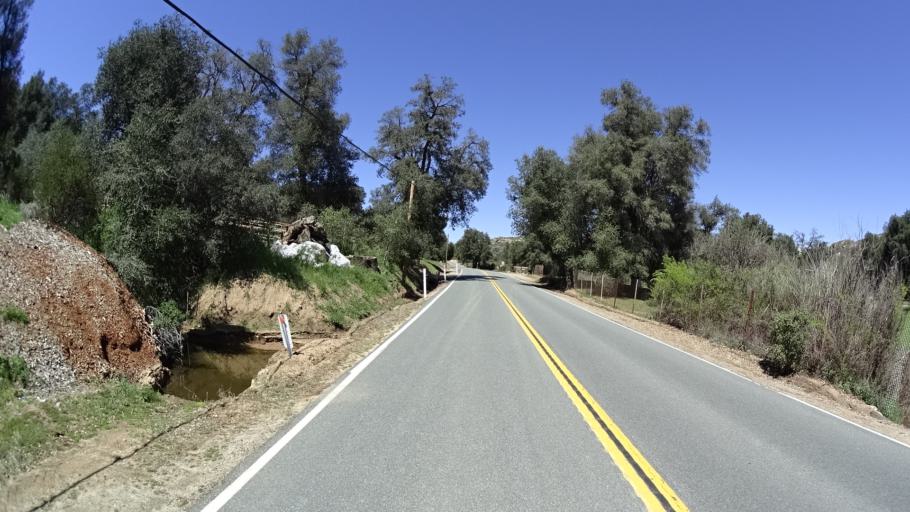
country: US
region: California
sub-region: San Diego County
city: Descanso
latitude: 32.8882
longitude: -116.5759
